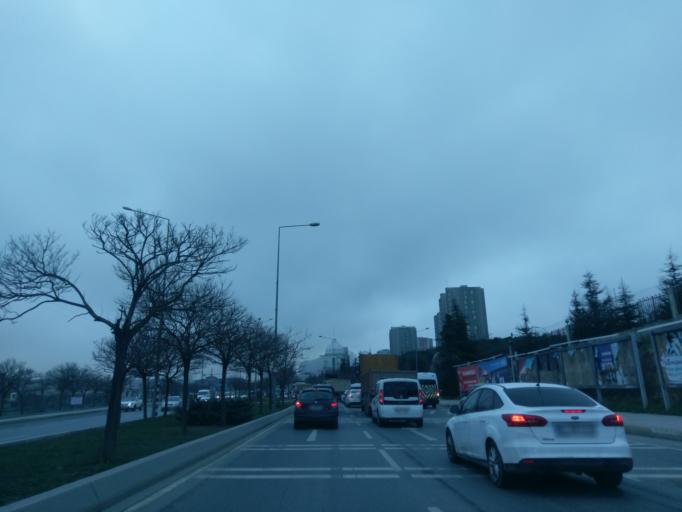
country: TR
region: Istanbul
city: Mahmutbey
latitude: 41.0461
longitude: 28.7742
